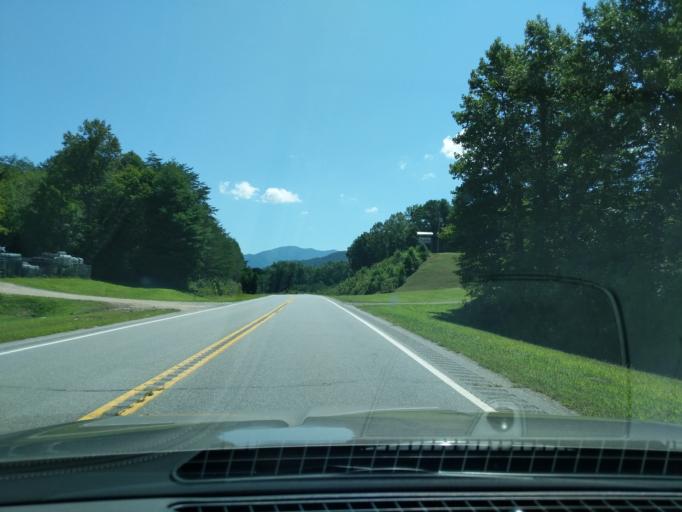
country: US
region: Georgia
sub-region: Towns County
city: Hiawassee
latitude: 35.0287
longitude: -83.7231
